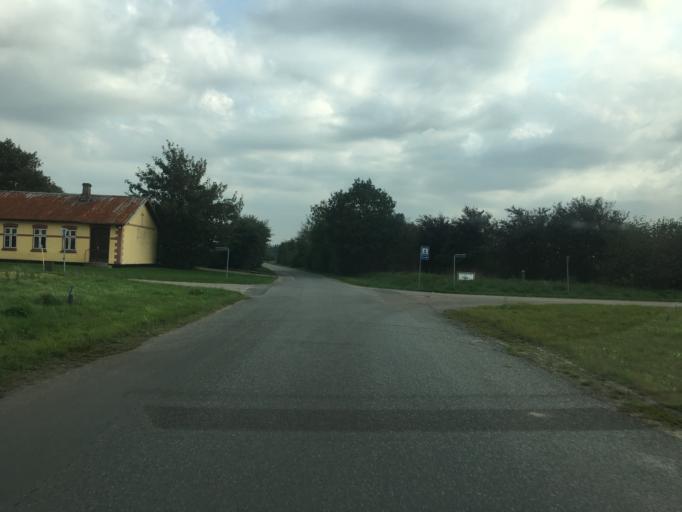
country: DE
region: Schleswig-Holstein
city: Bramstedtlund
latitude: 54.9709
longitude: 9.0812
